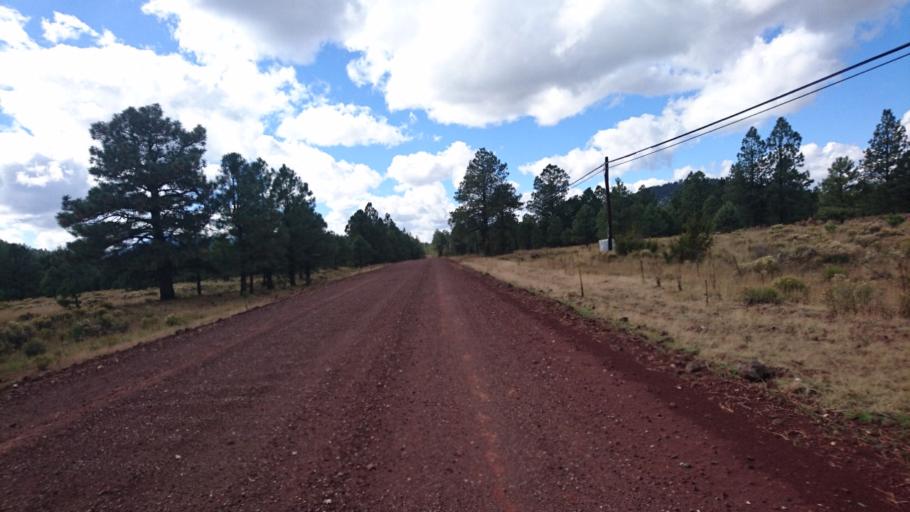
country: US
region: Arizona
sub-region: Coconino County
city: Williams
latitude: 35.2636
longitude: -112.0957
